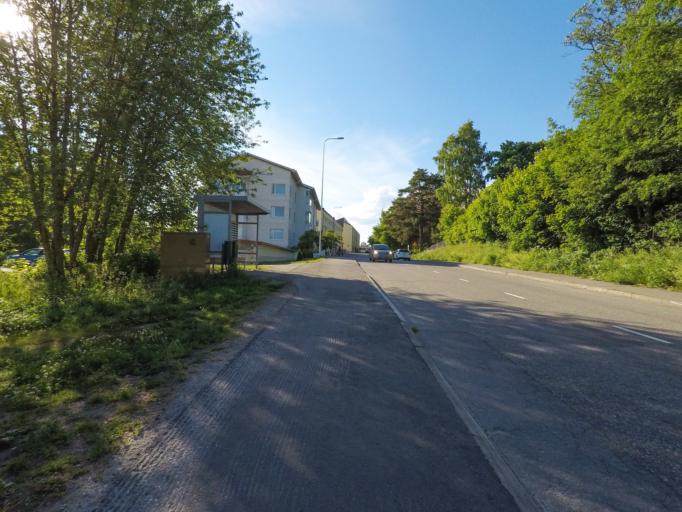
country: FI
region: Southern Savonia
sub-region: Savonlinna
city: Savonlinna
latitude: 61.8637
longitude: 28.8584
